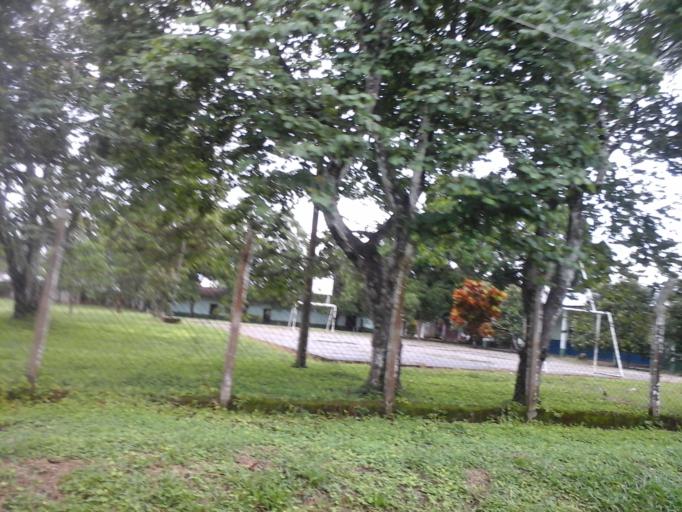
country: CO
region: Caqueta
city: El Doncello
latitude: 1.6127
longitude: -74.9968
